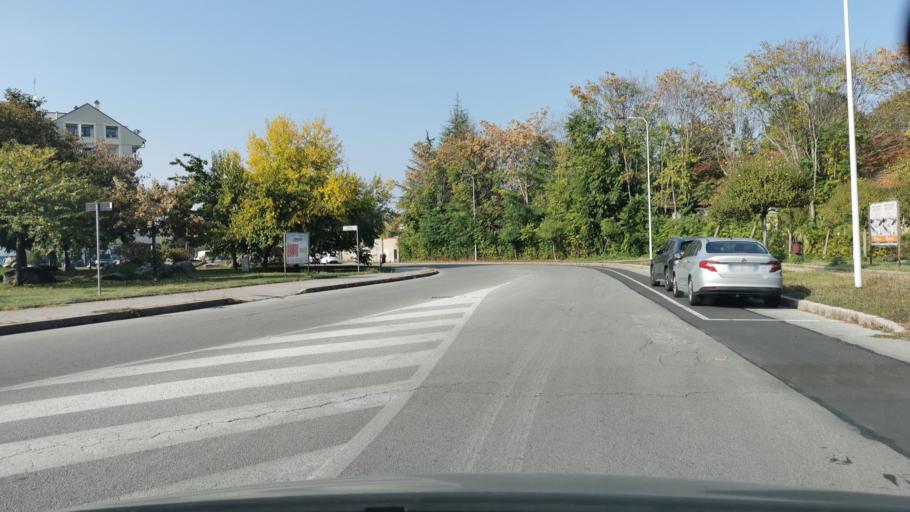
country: IT
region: Piedmont
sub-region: Provincia di Cuneo
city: Cuneo
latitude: 44.3722
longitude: 7.5357
